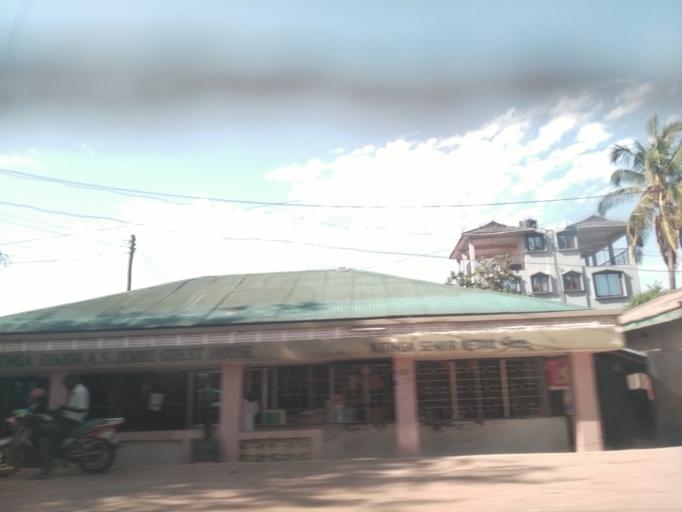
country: TZ
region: Mwanza
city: Mwanza
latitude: -2.5039
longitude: 32.8983
